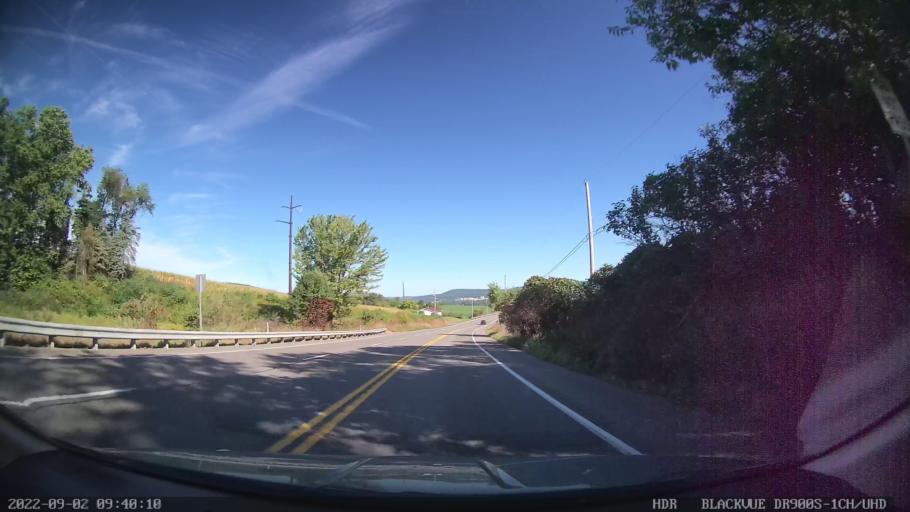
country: US
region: Pennsylvania
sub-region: Montour County
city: Mechanicsville
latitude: 40.9224
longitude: -76.5873
